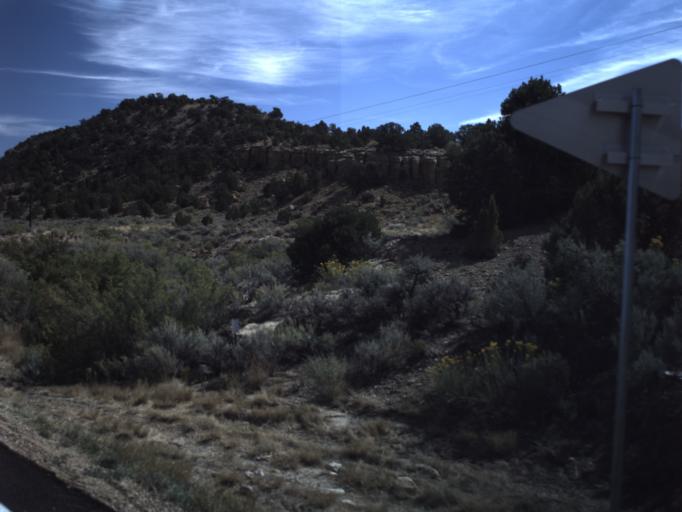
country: US
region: Utah
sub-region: Wayne County
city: Loa
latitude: 37.7699
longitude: -111.6640
